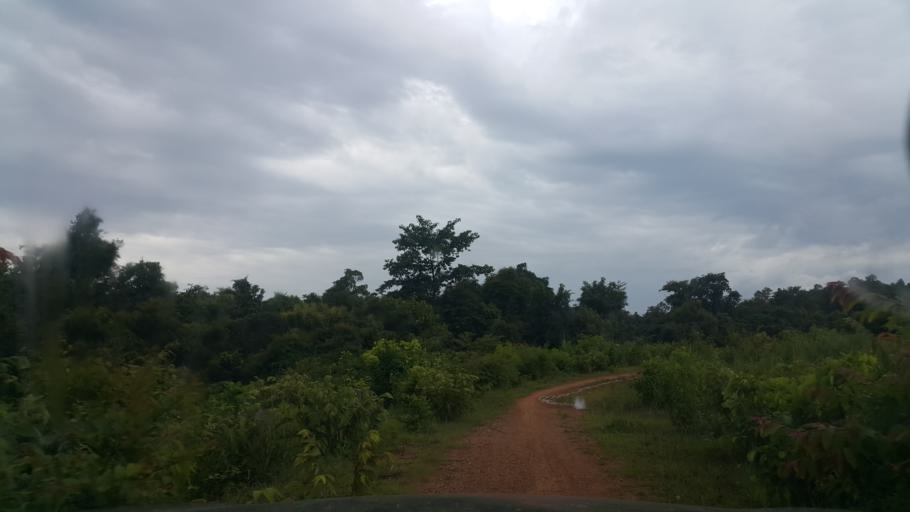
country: TH
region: Chiang Mai
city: San Sai
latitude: 19.0007
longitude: 99.1326
